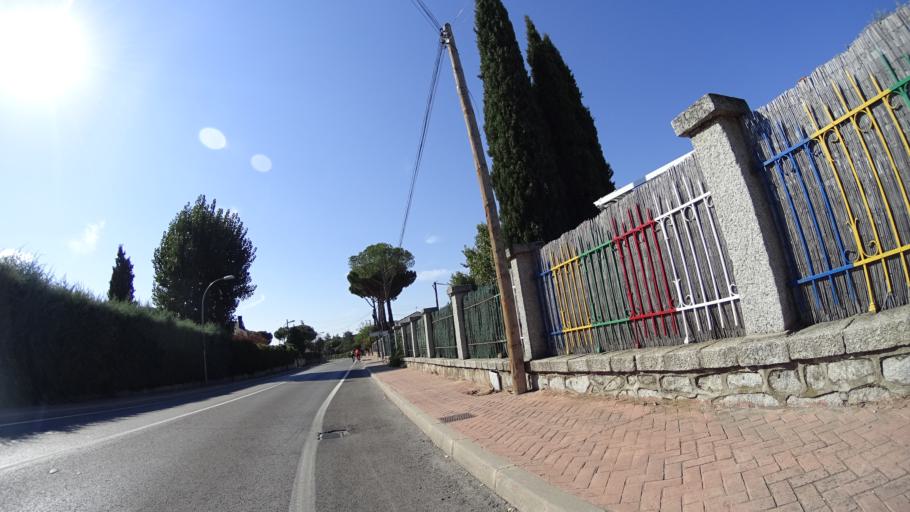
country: ES
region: Madrid
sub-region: Provincia de Madrid
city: Collado-Villalba
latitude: 40.6161
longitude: -4.0062
